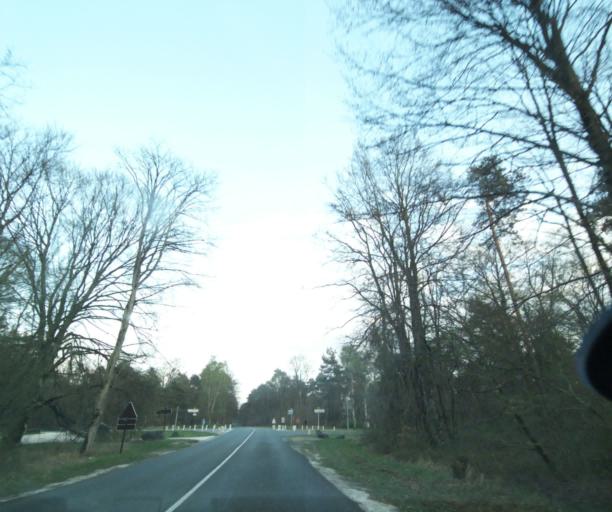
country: FR
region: Ile-de-France
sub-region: Departement de Seine-et-Marne
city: Avon
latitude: 48.3769
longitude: 2.7388
